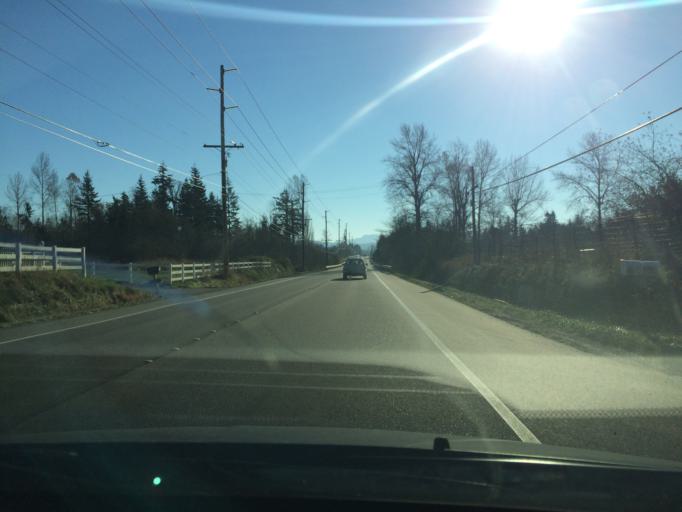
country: US
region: Washington
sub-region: Whatcom County
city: Bellingham
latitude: 48.7983
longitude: -122.4428
